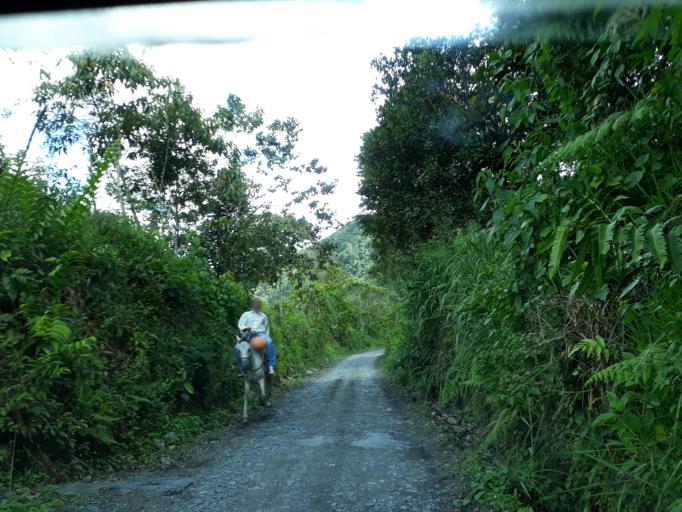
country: CO
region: Boyaca
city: Quipama
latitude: 5.4049
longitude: -74.1997
